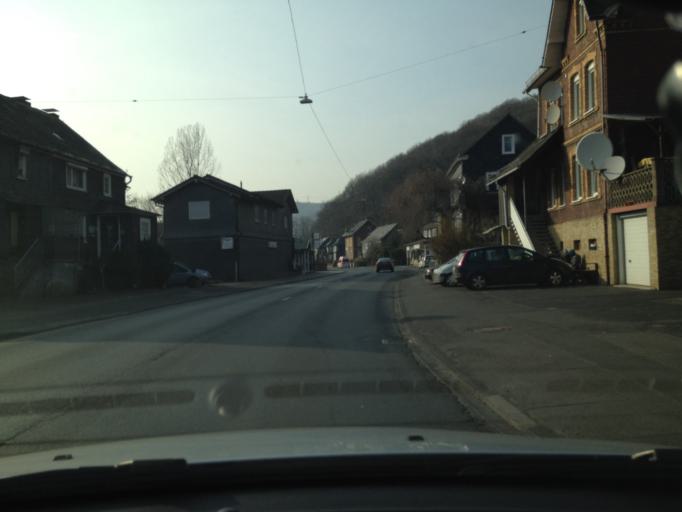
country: DE
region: Rheinland-Pfalz
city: Herdorf
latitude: 50.7825
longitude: 7.9784
